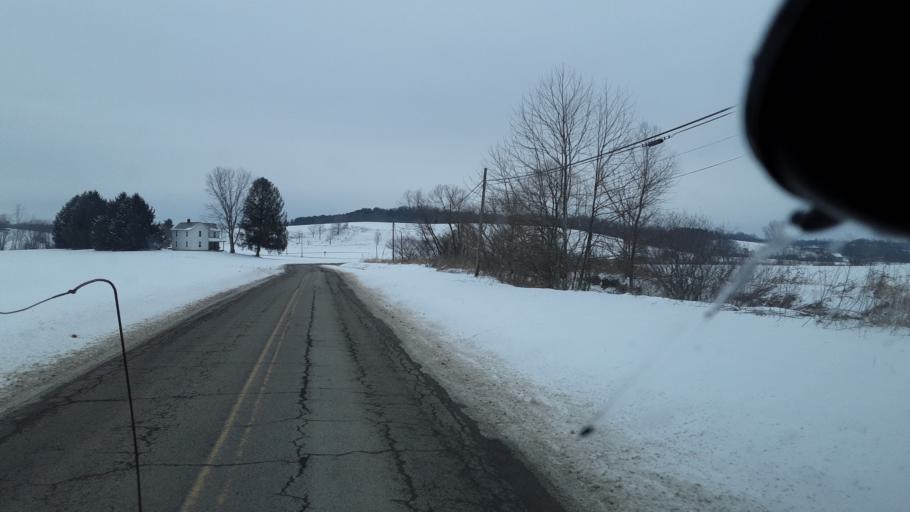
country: US
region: Ohio
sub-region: Perry County
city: Somerset
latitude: 39.8836
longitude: -82.2166
